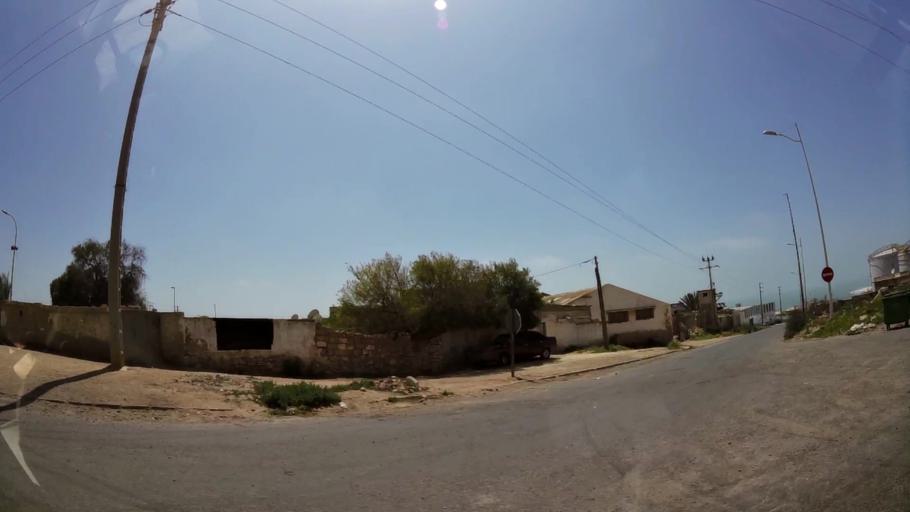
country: MA
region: Souss-Massa-Draa
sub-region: Agadir-Ida-ou-Tnan
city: Agadir
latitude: 30.4366
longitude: -9.6432
